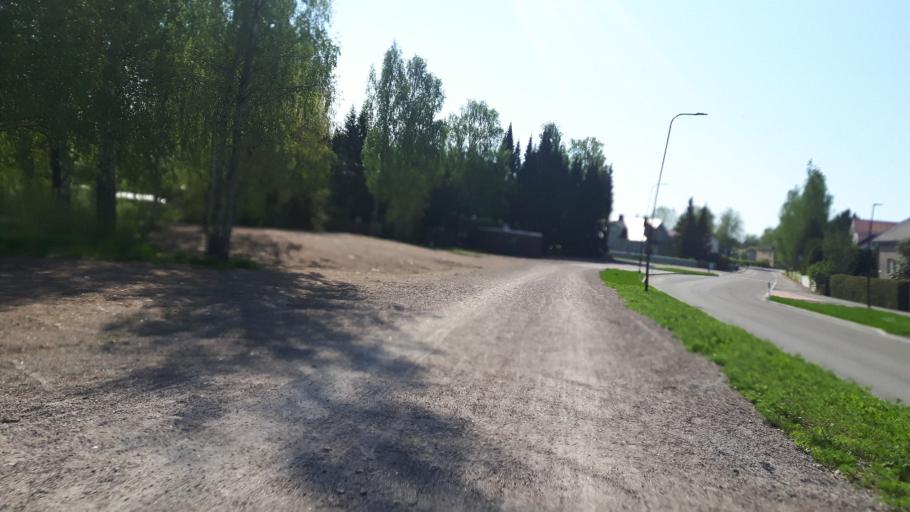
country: FI
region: Uusimaa
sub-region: Loviisa
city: Lovisa
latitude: 60.4485
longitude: 26.2358
